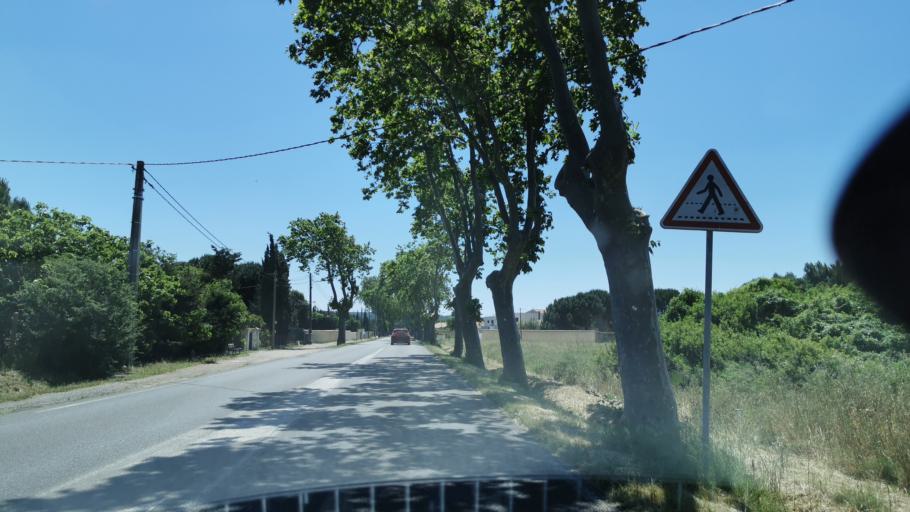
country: FR
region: Languedoc-Roussillon
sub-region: Departement de l'Aude
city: Saint-Marcel-sur-Aude
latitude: 43.2522
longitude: 2.9141
